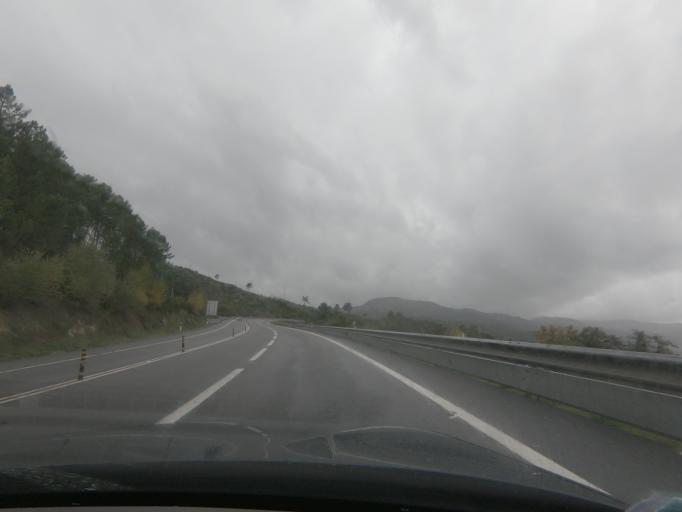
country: PT
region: Vila Real
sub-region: Vila Real
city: Vila Real
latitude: 41.2766
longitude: -7.7942
